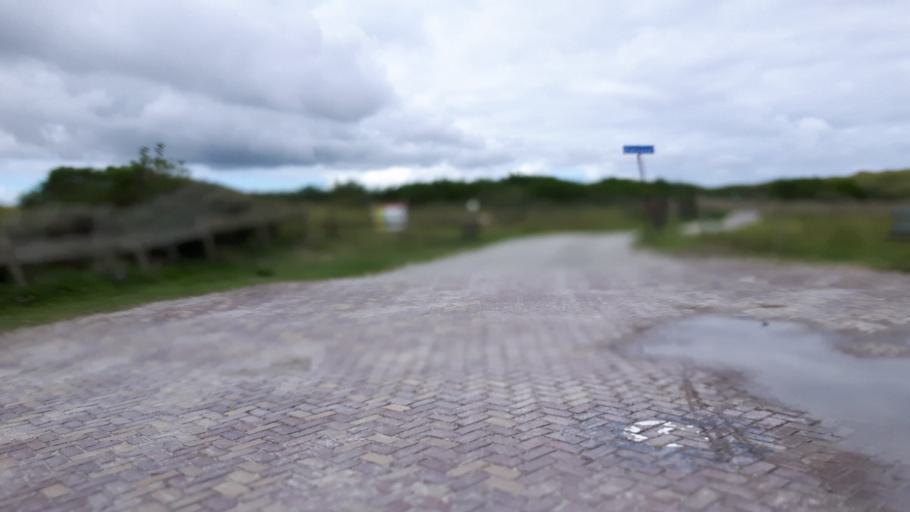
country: NL
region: Friesland
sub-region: Gemeente Ameland
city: Nes
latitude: 53.4576
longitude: 5.7580
